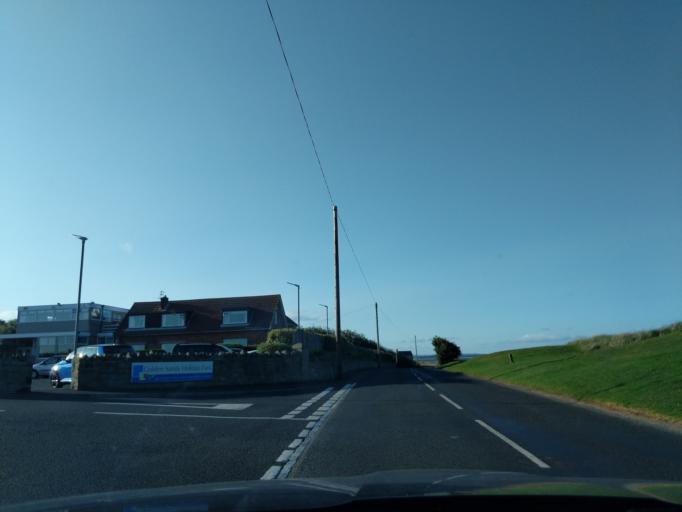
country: GB
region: England
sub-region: Northumberland
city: Lynemouth
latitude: 55.2310
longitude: -1.5327
